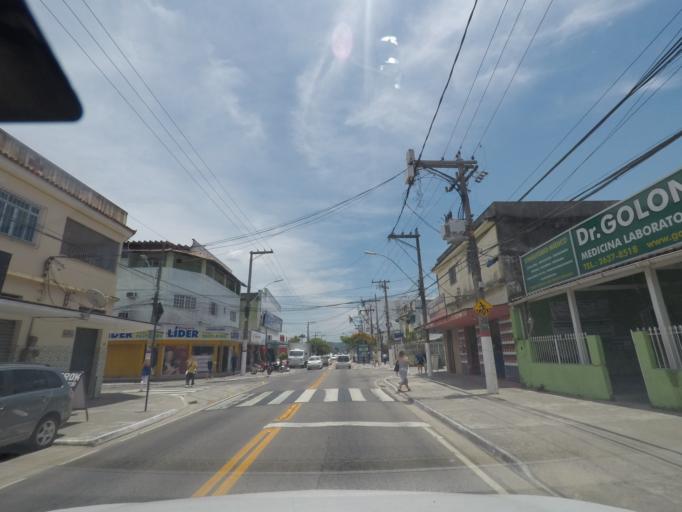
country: BR
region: Rio de Janeiro
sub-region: Marica
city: Marica
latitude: -22.9221
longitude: -42.8173
